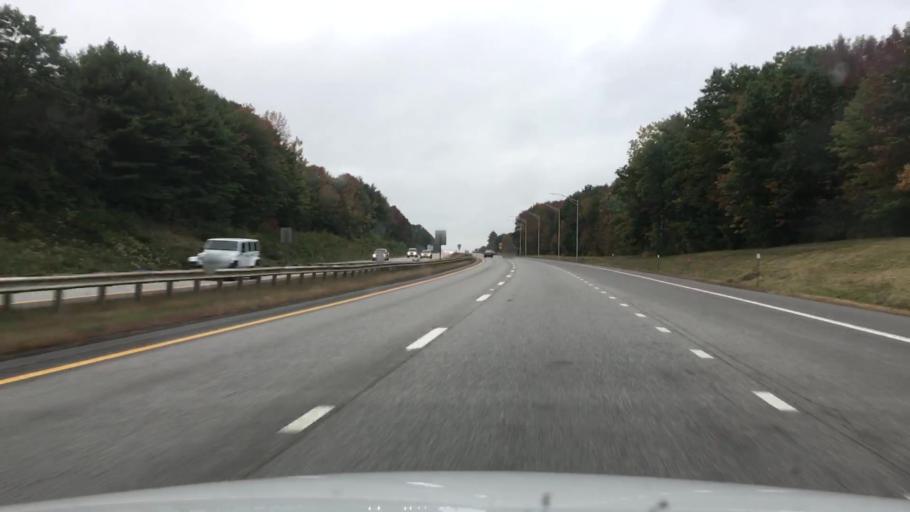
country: US
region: Maine
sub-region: Cumberland County
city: Falmouth
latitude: 43.7351
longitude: -70.3018
